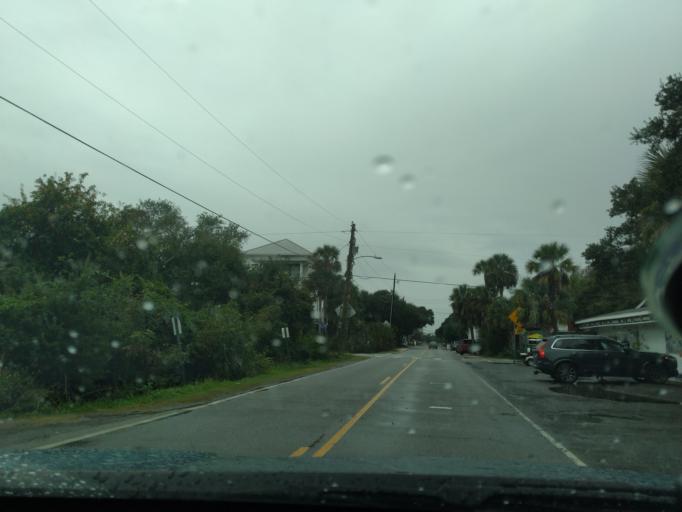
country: US
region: South Carolina
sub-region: Charleston County
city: Folly Beach
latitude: 32.6567
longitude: -79.9381
